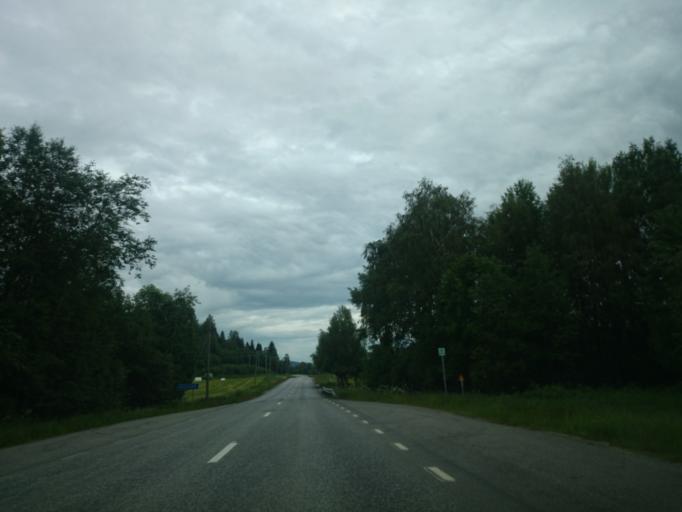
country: SE
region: Vaesternorrland
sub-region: Sundsvalls Kommun
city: Vi
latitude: 62.4485
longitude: 17.1654
